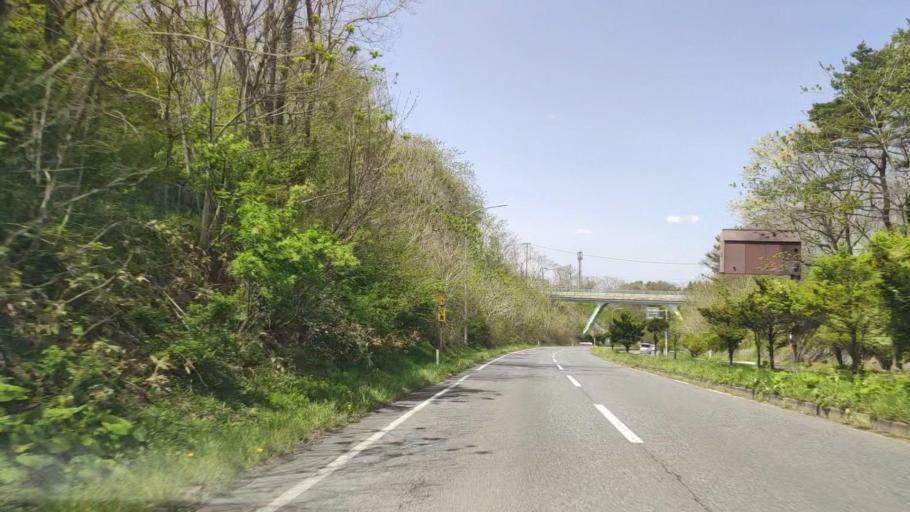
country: JP
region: Aomori
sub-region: Hachinohe Shi
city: Uchimaru
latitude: 40.4958
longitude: 141.4605
